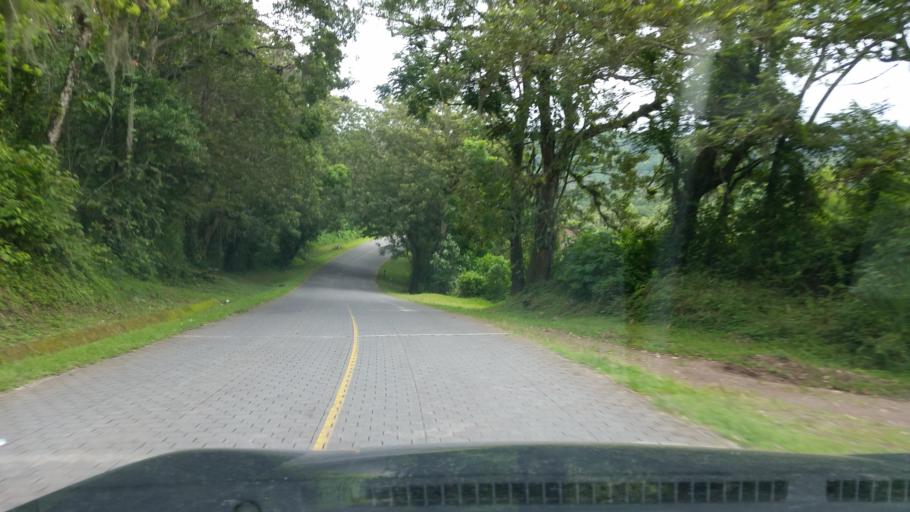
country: NI
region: Jinotega
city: Jinotega
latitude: 13.1904
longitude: -85.7324
